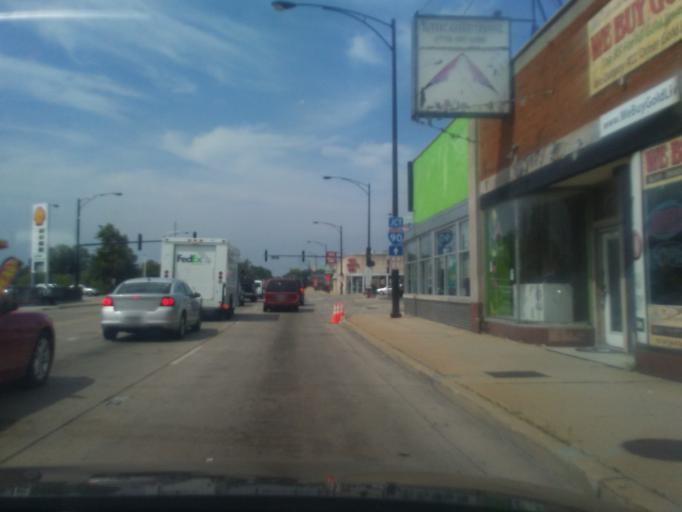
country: US
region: Illinois
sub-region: Cook County
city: Harwood Heights
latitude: 41.9803
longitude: -87.8069
